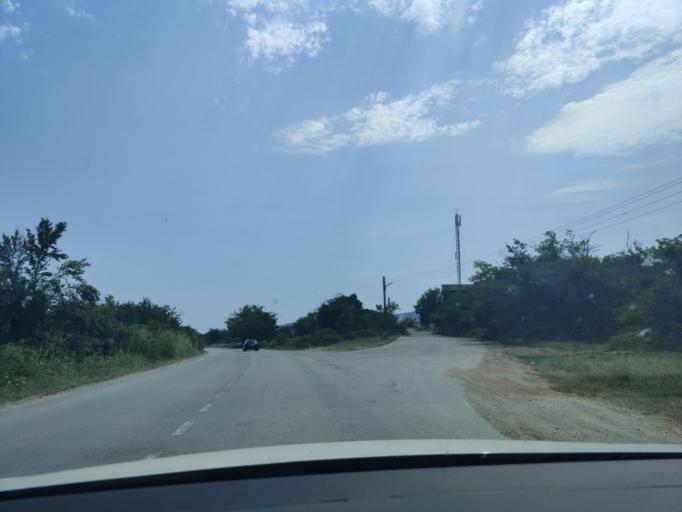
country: BG
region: Montana
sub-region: Obshtina Chiprovtsi
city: Chiprovtsi
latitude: 43.5051
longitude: 22.9859
